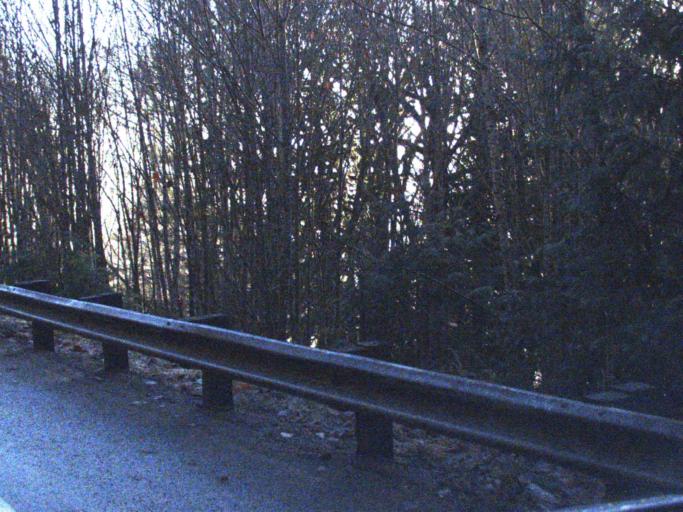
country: US
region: Washington
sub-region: Snohomish County
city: Darrington
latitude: 48.4878
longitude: -121.6043
